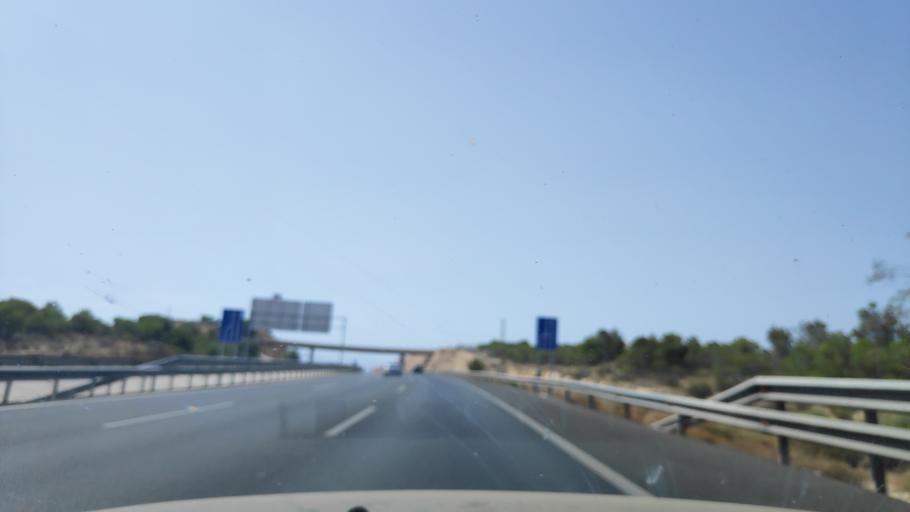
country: ES
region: Murcia
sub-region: Murcia
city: Molina de Segura
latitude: 38.0451
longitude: -1.1656
